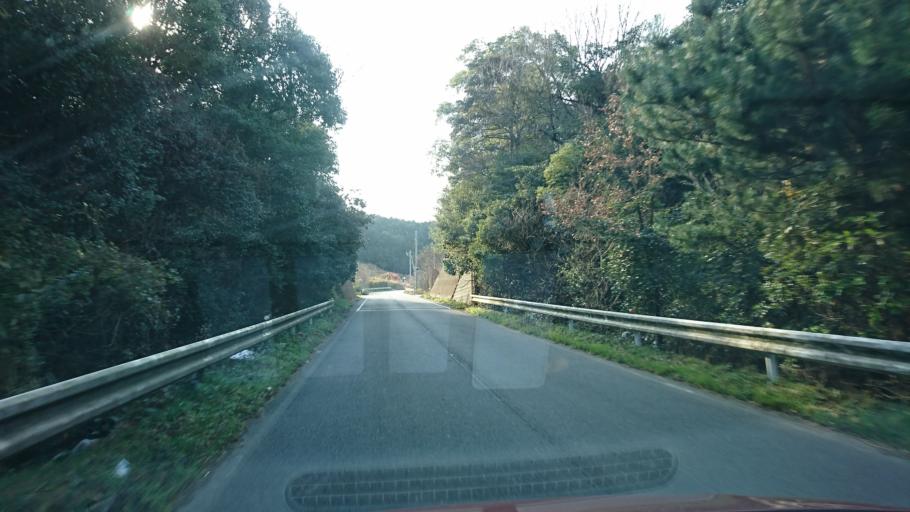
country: JP
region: Ehime
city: Hojo
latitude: 34.0206
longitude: 132.9795
